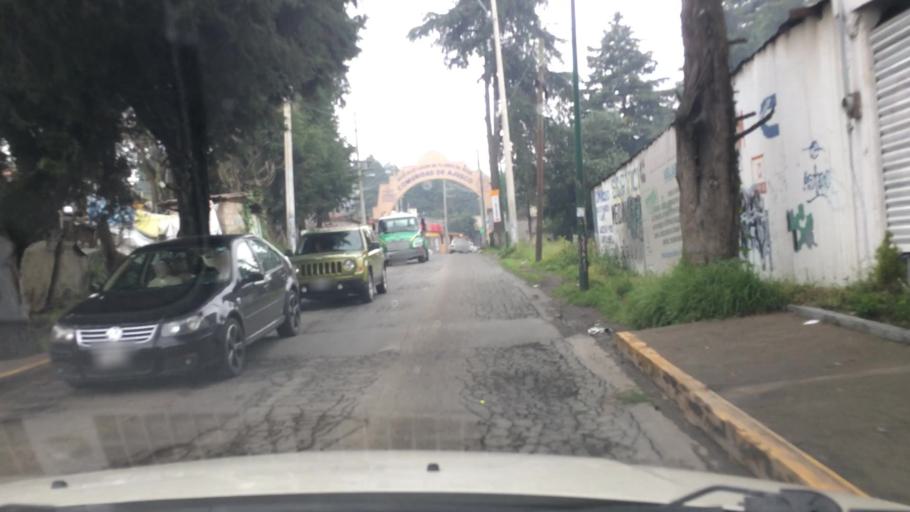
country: MX
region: Mexico City
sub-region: Tlalpan
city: Lomas de Tepemecatl
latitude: 19.2312
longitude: -99.1935
